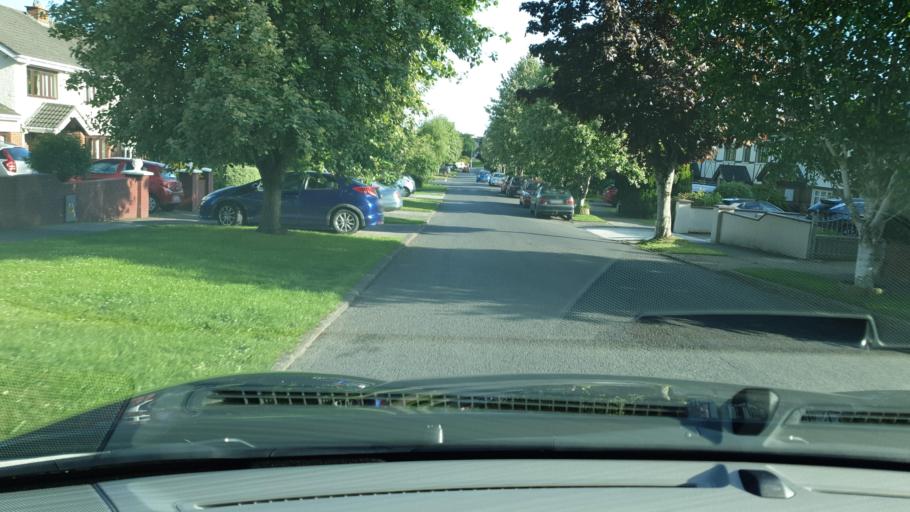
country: IE
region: Leinster
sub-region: An Mhi
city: Ashbourne
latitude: 53.5167
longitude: -6.4017
